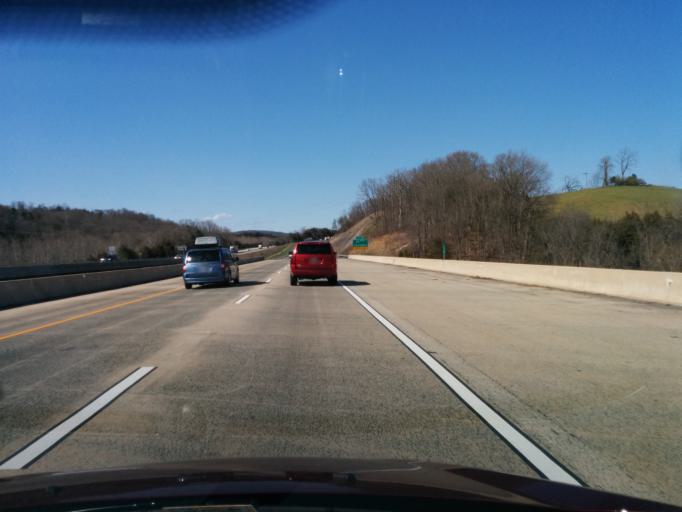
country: US
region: Virginia
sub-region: Rockbridge County
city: East Lexington
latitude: 37.7780
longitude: -79.4005
